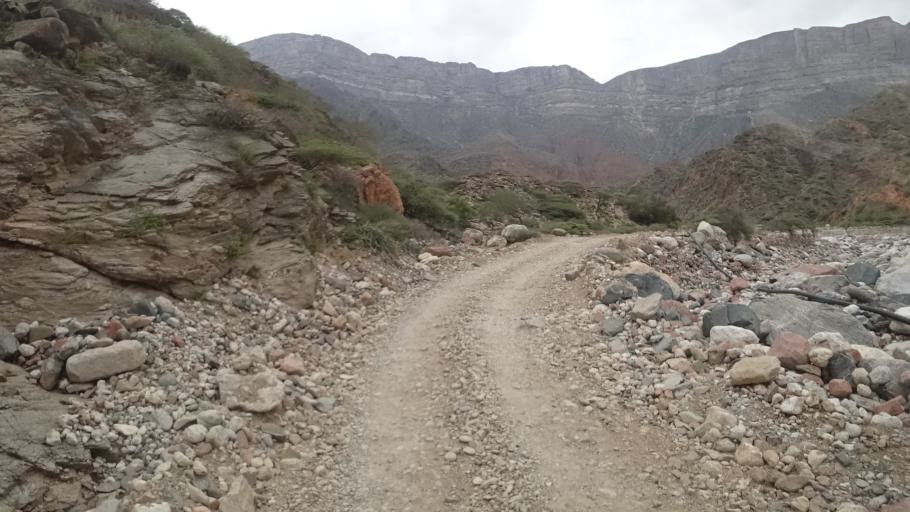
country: OM
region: Zufar
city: Salalah
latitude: 17.1821
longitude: 54.9455
